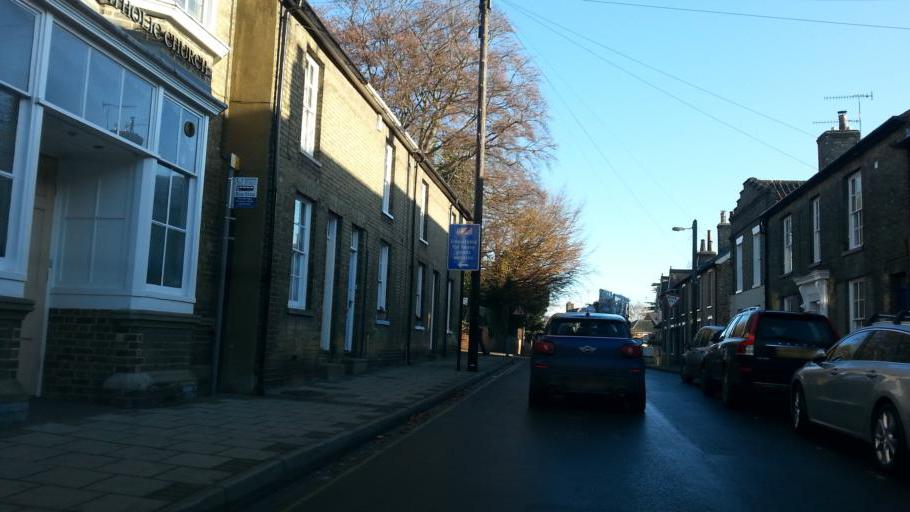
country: GB
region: England
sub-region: Suffolk
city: Woodbridge
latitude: 52.0944
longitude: 1.3188
